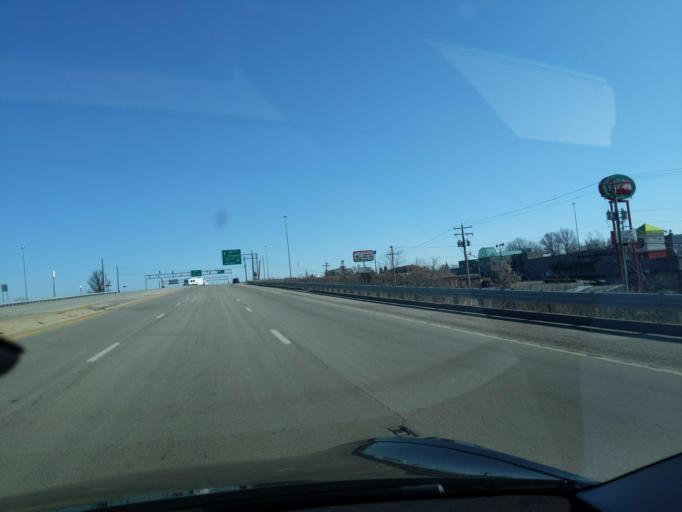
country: US
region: Kentucky
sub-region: Clark County
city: Winchester
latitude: 38.0083
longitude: -84.2100
